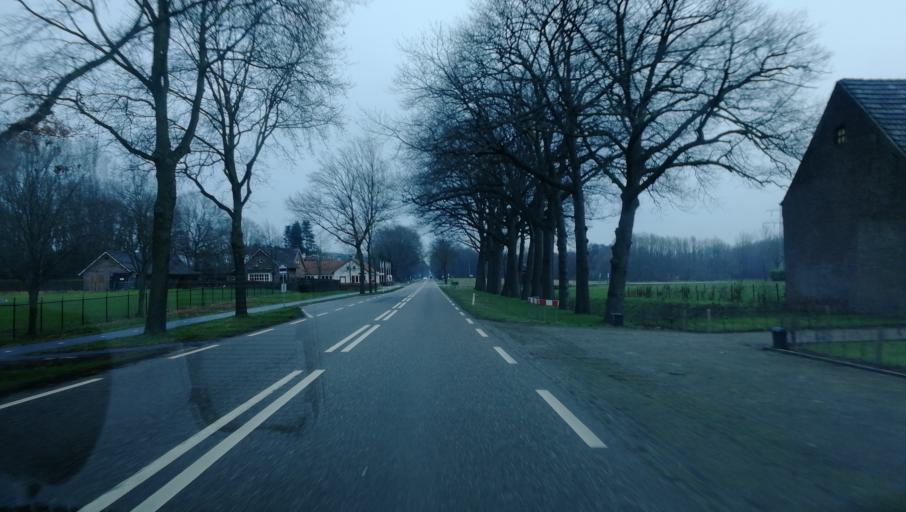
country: NL
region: Limburg
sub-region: Gemeente Beesel
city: Reuver
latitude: 51.3090
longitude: 6.0666
